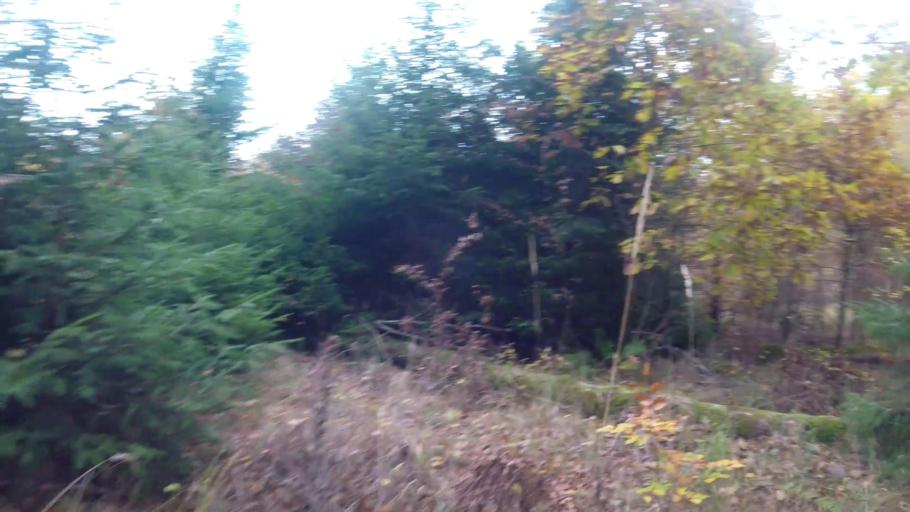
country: DE
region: Baden-Wuerttemberg
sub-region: Regierungsbezirk Stuttgart
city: Kirchberg an der Murr
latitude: 48.9825
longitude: 9.3550
